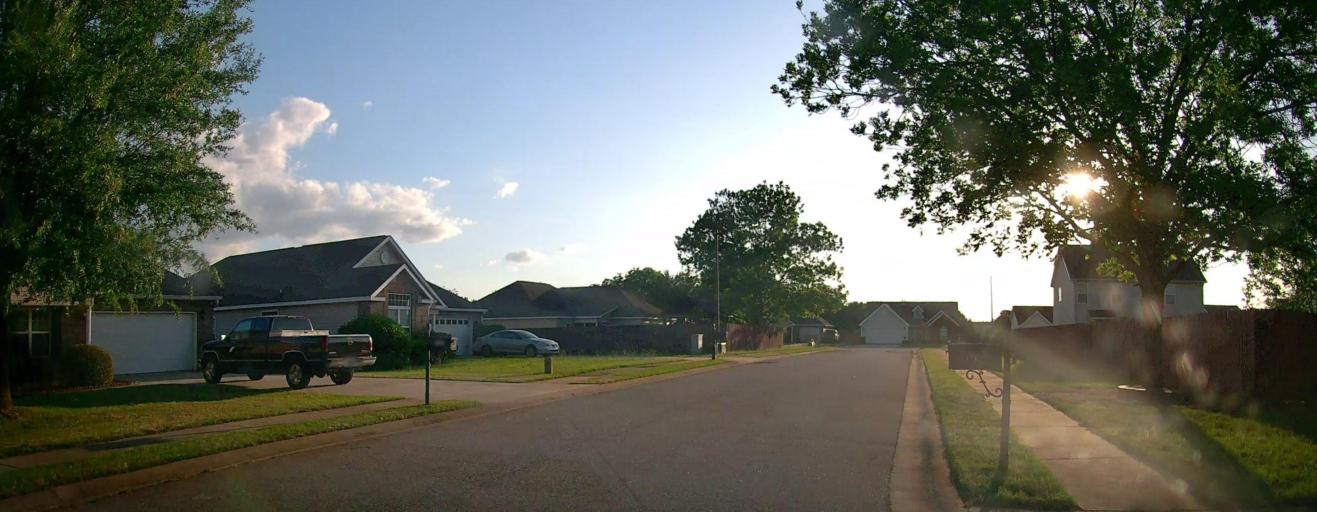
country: US
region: Georgia
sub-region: Houston County
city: Centerville
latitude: 32.6270
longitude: -83.7116
